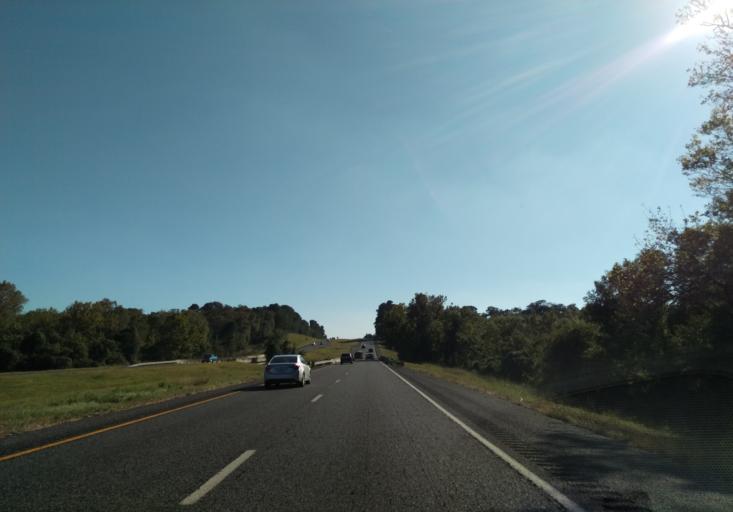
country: US
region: Texas
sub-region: Waller County
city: Hempstead
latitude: 30.2199
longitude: -96.0568
